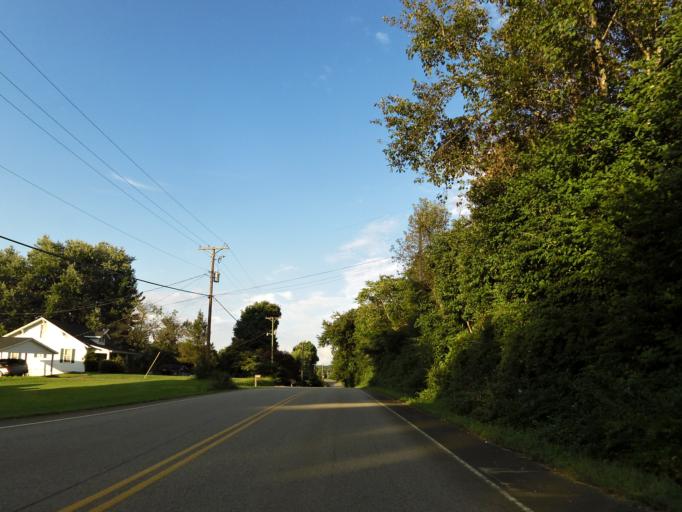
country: US
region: Tennessee
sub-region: Knox County
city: Mascot
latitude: 36.0442
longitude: -83.8116
